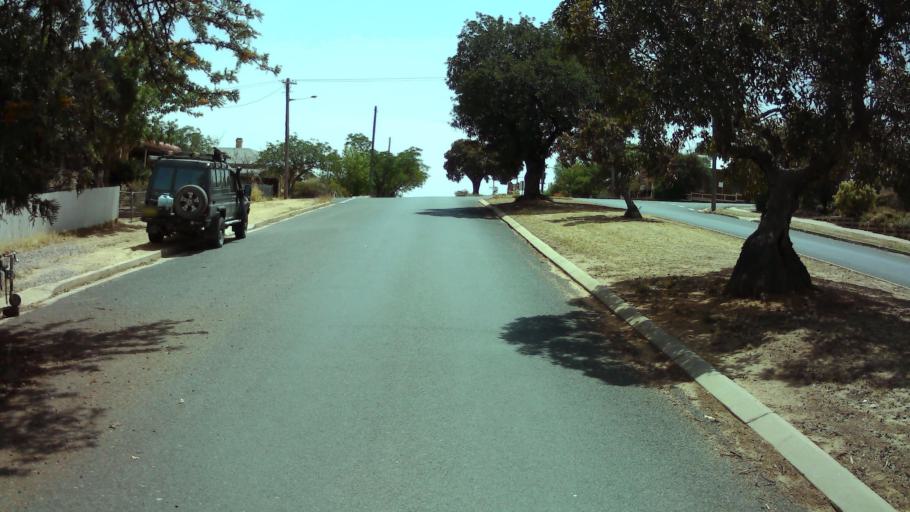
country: AU
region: New South Wales
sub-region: Weddin
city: Grenfell
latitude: -33.8967
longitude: 148.1599
